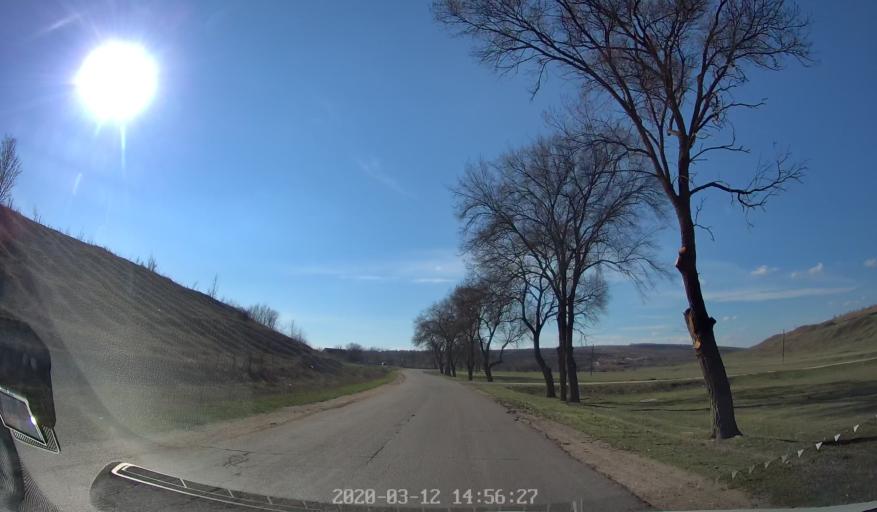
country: MD
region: Telenesti
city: Cocieri
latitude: 47.2250
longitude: 29.0491
